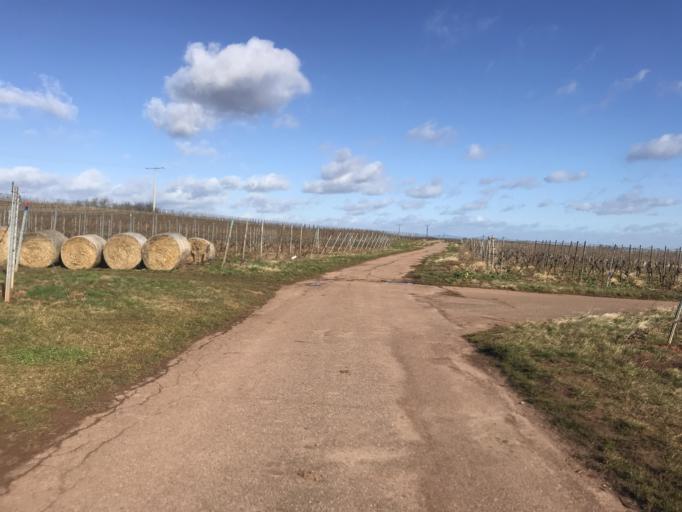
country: DE
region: Rheinland-Pfalz
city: Nackenheim
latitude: 49.8974
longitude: 8.3360
